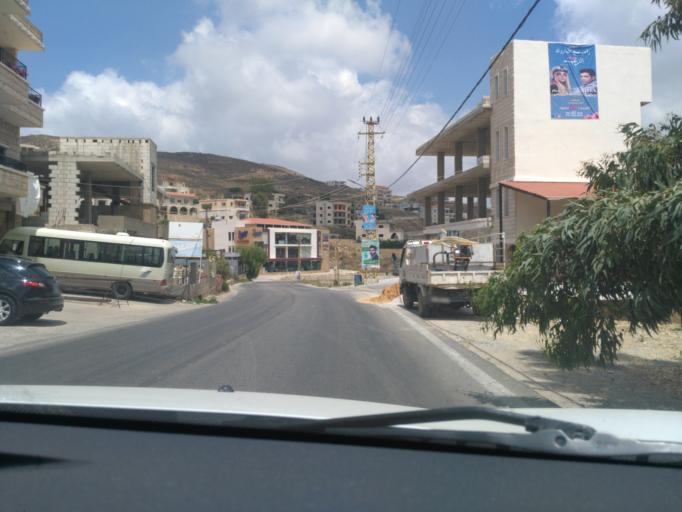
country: LB
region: Mont-Liban
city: Beit ed Dine
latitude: 33.7034
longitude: 35.6631
